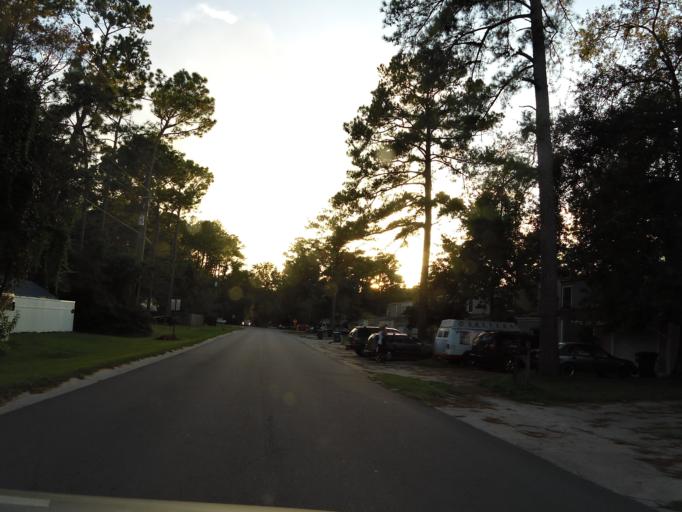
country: US
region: Georgia
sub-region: Camden County
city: Kingsland
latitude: 30.7941
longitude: -81.6928
